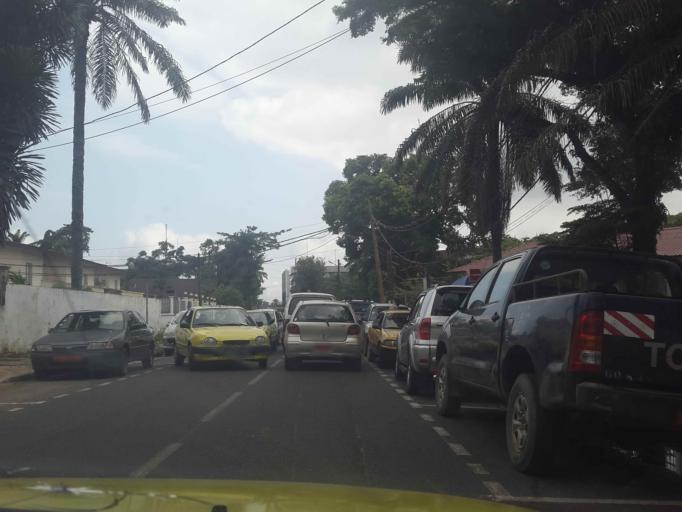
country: CM
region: Littoral
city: Douala
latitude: 4.0379
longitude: 9.6886
